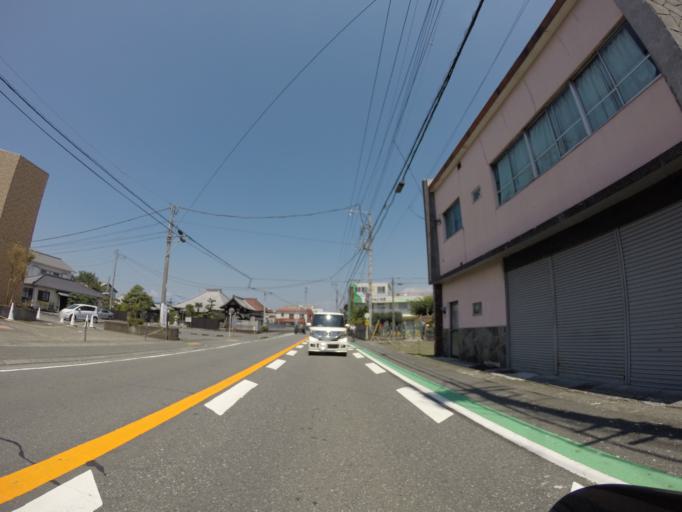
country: JP
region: Shizuoka
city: Fuji
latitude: 35.1531
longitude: 138.6622
